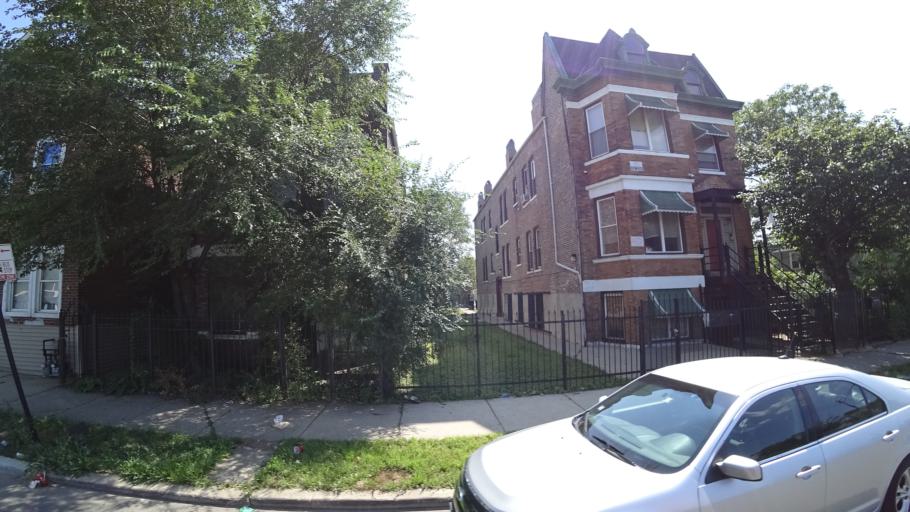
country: US
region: Illinois
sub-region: Cook County
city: Cicero
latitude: 41.8587
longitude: -87.7279
